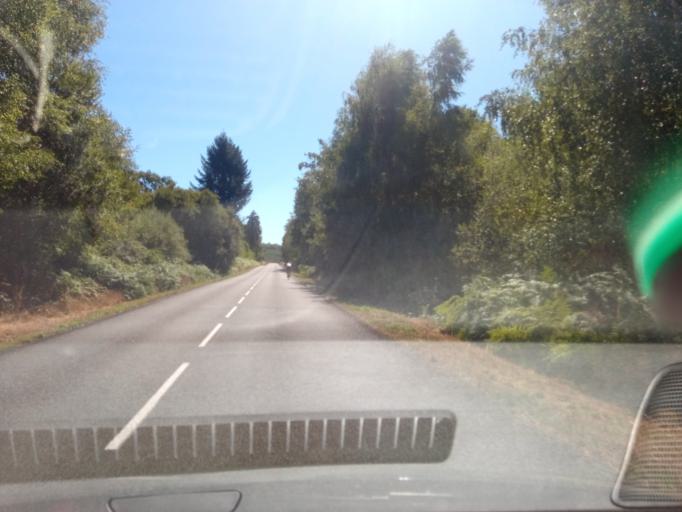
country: FR
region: Limousin
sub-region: Departement de la Haute-Vienne
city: Nantiat
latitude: 46.0675
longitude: 1.2041
